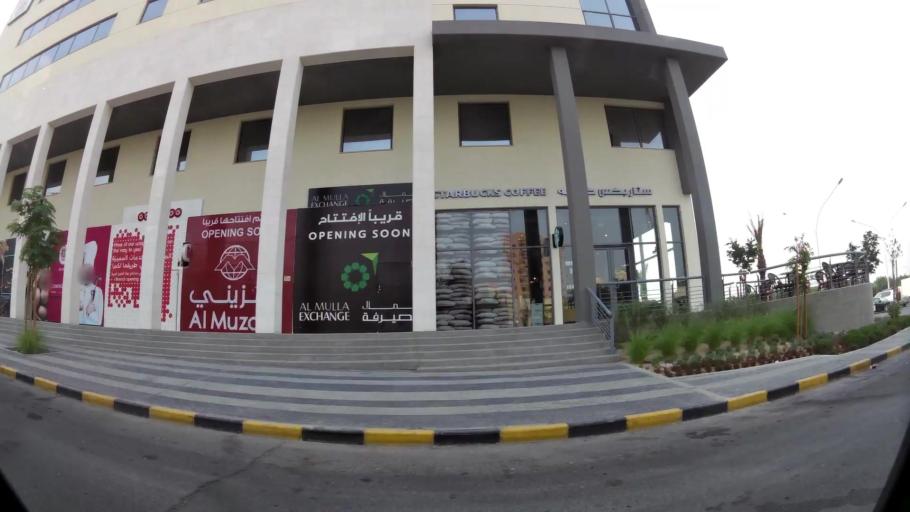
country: KW
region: Al Farwaniyah
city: Al Farwaniyah
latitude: 29.2952
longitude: 47.9665
